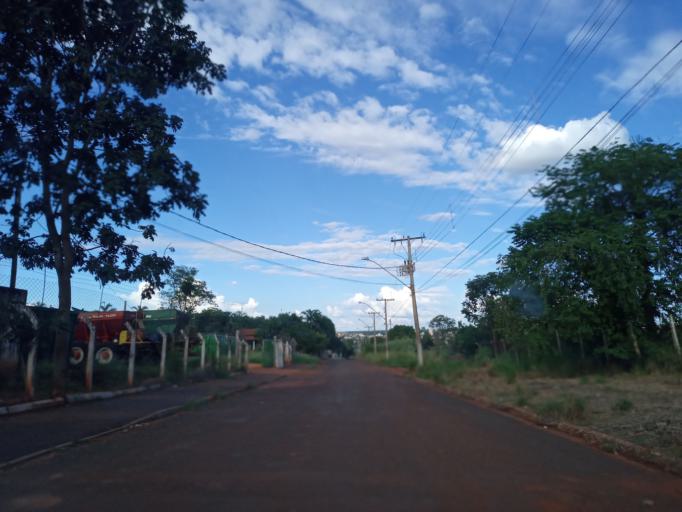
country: BR
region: Minas Gerais
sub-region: Ituiutaba
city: Ituiutaba
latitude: -18.9645
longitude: -49.4945
